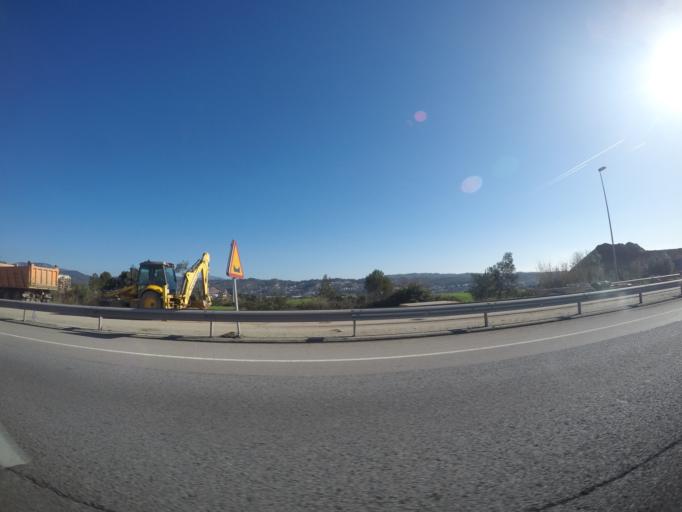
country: ES
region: Catalonia
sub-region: Provincia de Barcelona
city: Abrera
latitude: 41.5109
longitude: 1.9014
